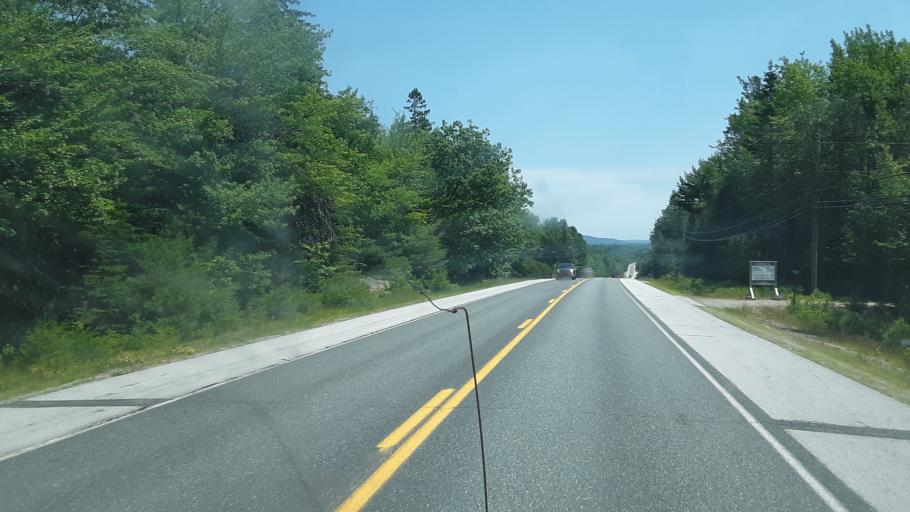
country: US
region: Maine
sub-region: Hancock County
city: Hancock
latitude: 44.5369
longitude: -68.2841
